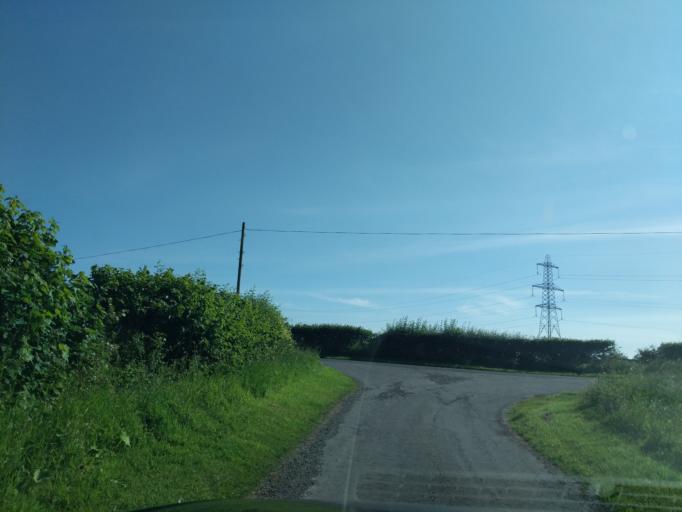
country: GB
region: Scotland
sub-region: East Lothian
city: Ormiston
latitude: 55.8771
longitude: -2.9346
